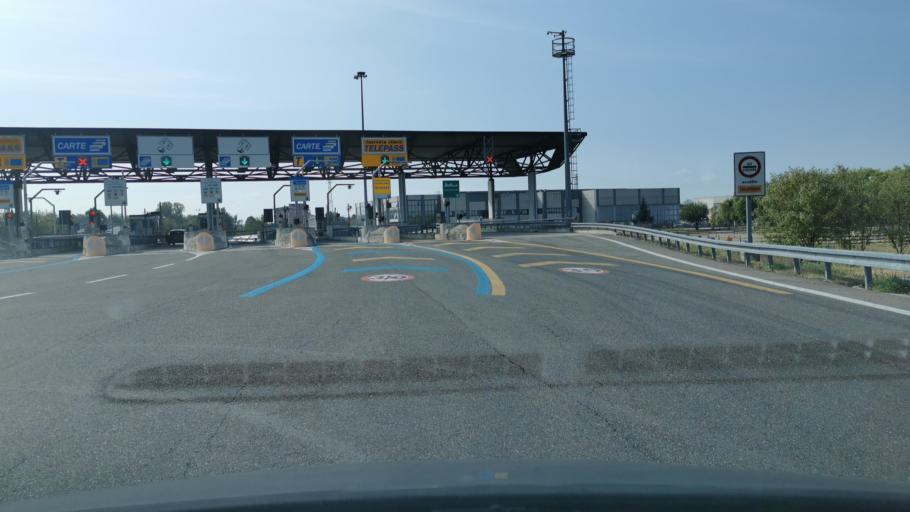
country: IT
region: Lombardy
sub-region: Provincia di Lodi
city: San Rocco al Porto
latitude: 45.0600
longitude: 9.6587
